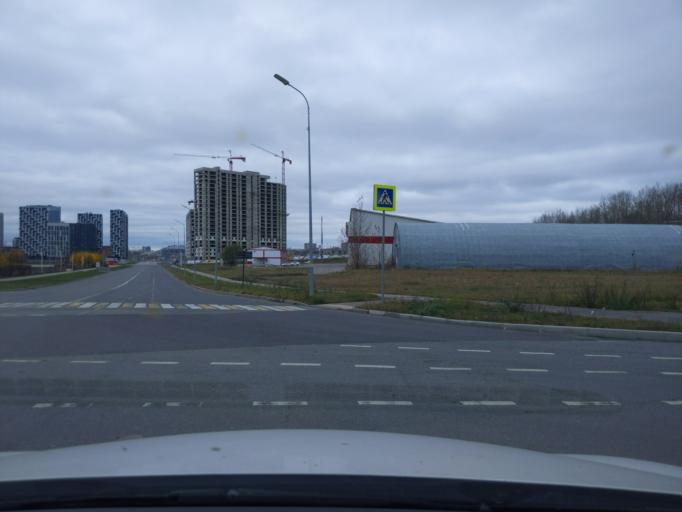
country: RU
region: Moscow
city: Pokrovskoye-Streshnevo
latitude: 55.8195
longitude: 37.4448
